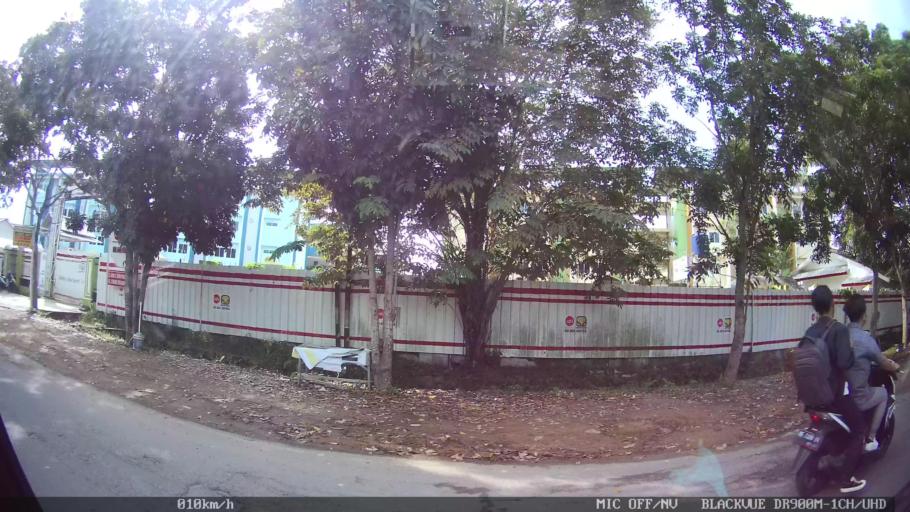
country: ID
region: Lampung
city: Kedaton
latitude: -5.3780
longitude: 105.3040
